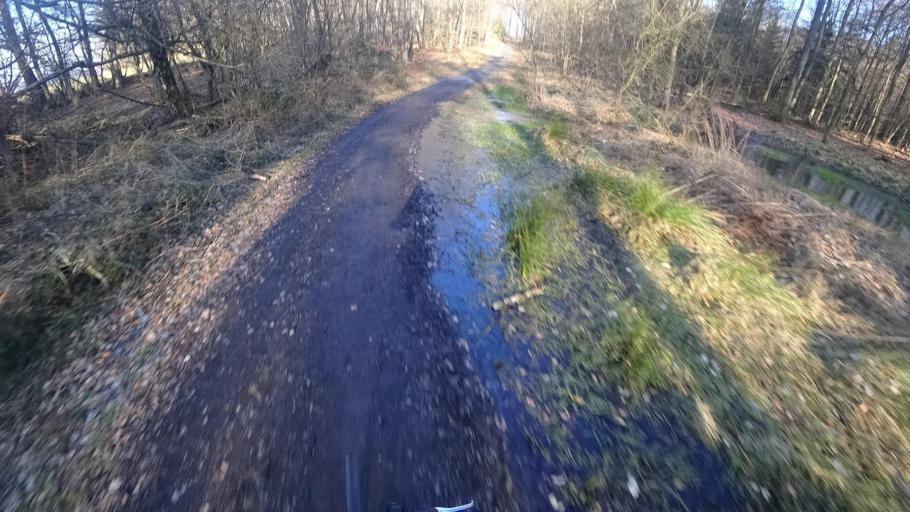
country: DE
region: Rheinland-Pfalz
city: Waldesch
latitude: 50.2640
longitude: 7.5338
